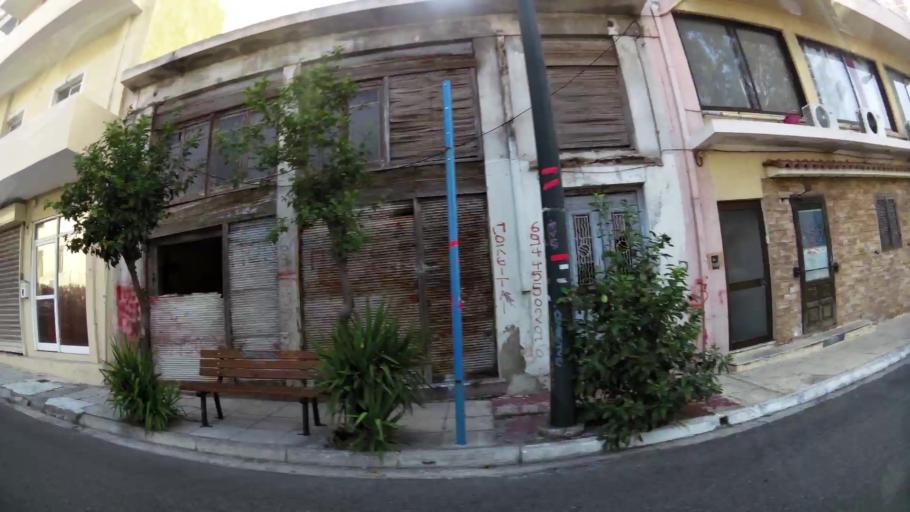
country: GR
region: Attica
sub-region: Nomos Piraios
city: Drapetsona
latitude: 37.9447
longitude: 23.6215
